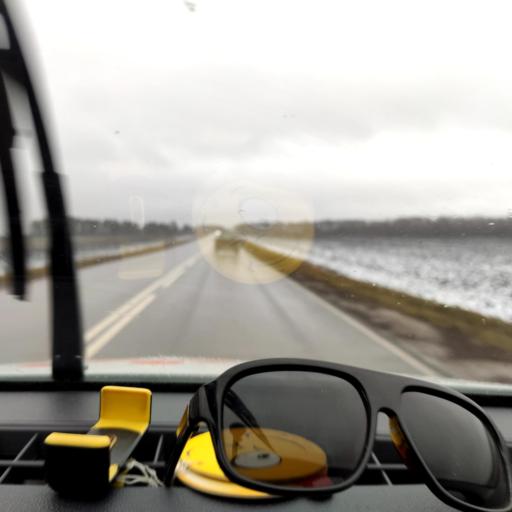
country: RU
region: Bashkortostan
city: Iglino
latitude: 54.8776
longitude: 56.5342
